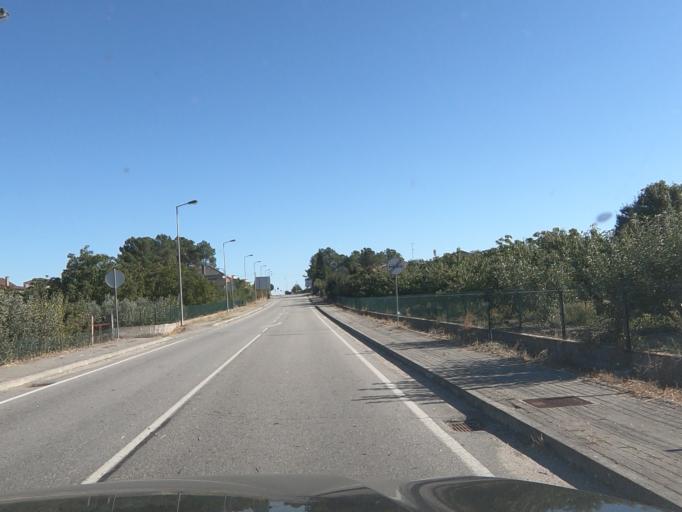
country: PT
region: Vila Real
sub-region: Valpacos
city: Valpacos
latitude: 41.6632
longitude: -7.3321
